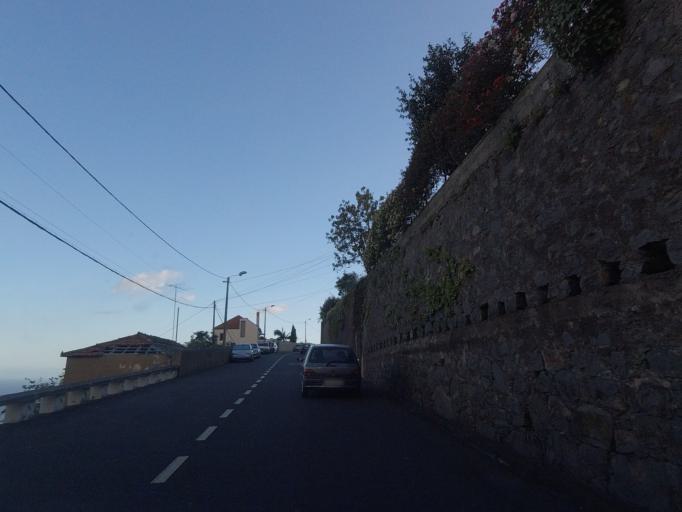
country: PT
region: Madeira
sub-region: Funchal
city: Nossa Senhora do Monte
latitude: 32.6718
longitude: -16.9316
